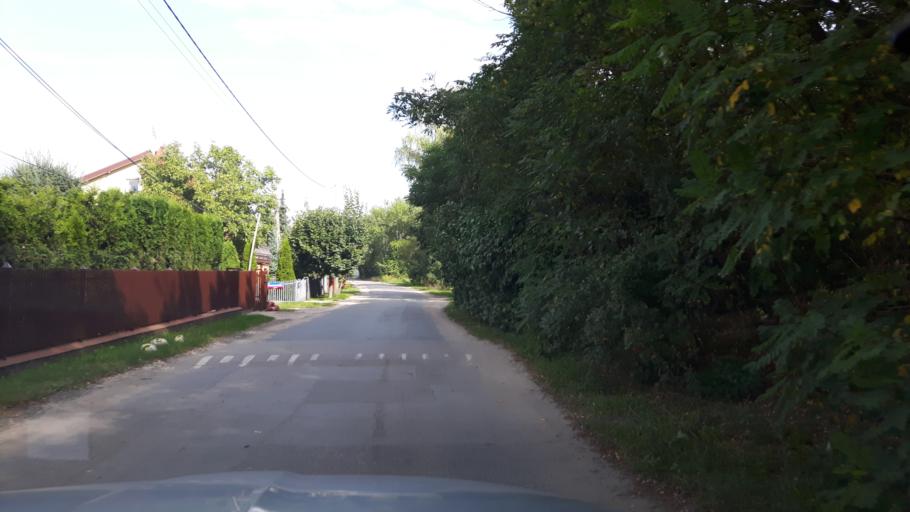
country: PL
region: Masovian Voivodeship
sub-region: Powiat wolominski
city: Marki
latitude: 52.3363
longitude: 21.0828
